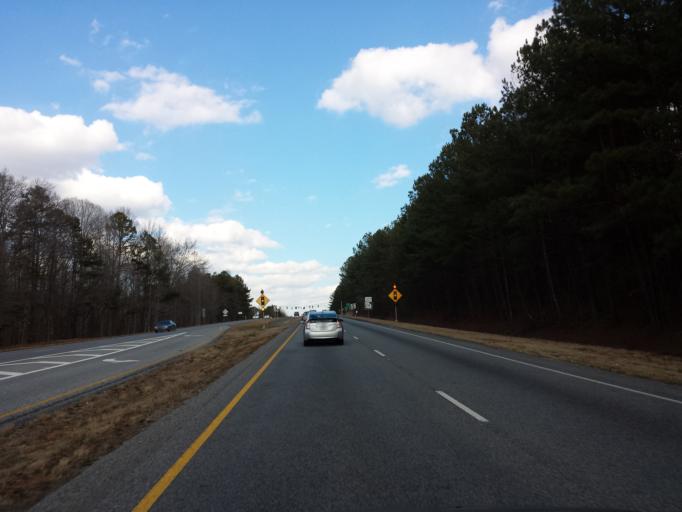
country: US
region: Georgia
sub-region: Dawson County
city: Dawsonville
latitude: 34.3966
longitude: -84.0150
